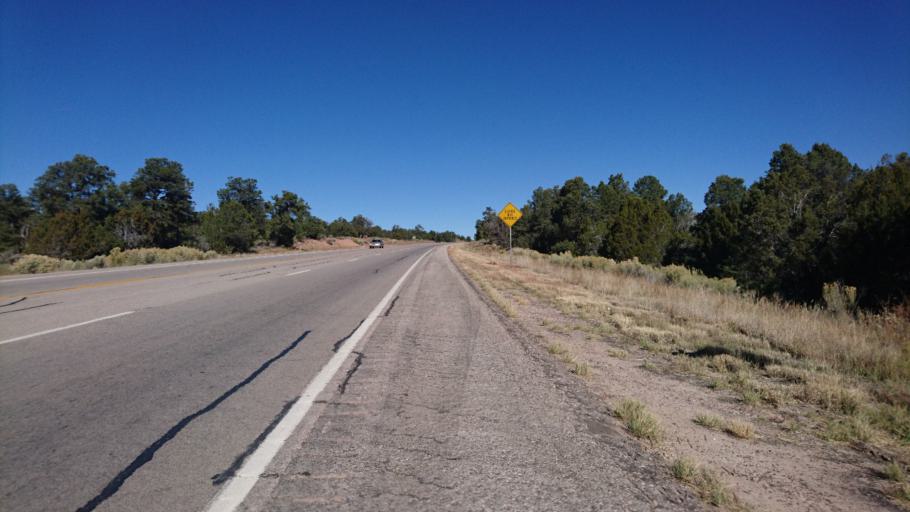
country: US
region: New Mexico
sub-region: McKinley County
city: Black Rock
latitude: 35.2223
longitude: -108.7657
